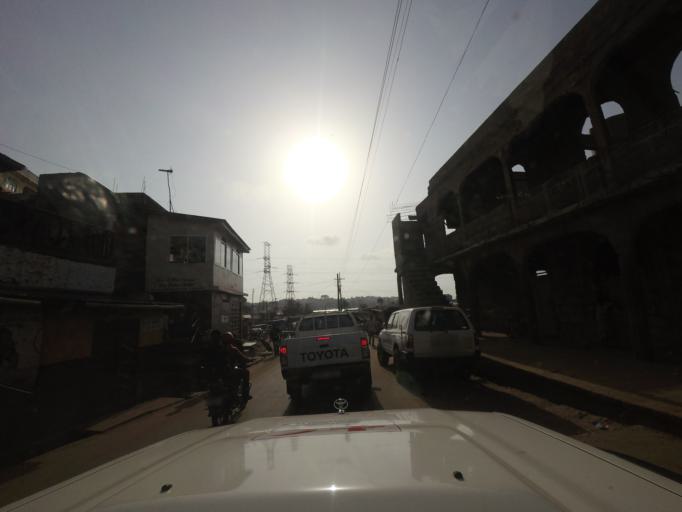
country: SL
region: Western Area
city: Freetown
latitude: 8.4850
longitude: -13.2495
